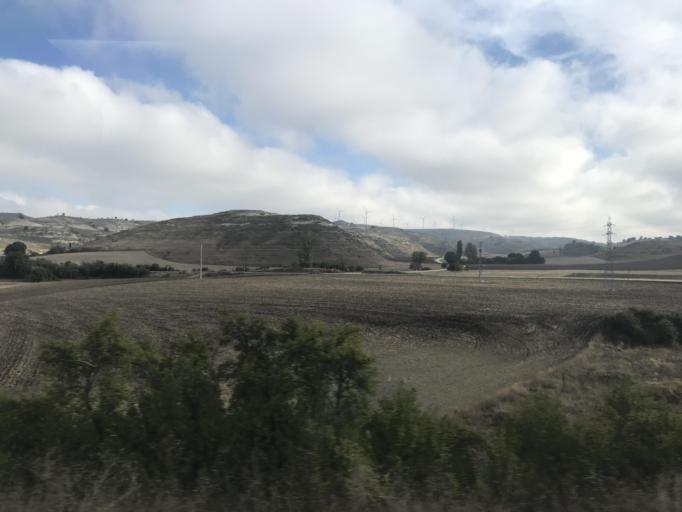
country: ES
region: Castille and Leon
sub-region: Provincia de Burgos
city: Santa Maria del Invierno
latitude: 42.4366
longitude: -3.4388
